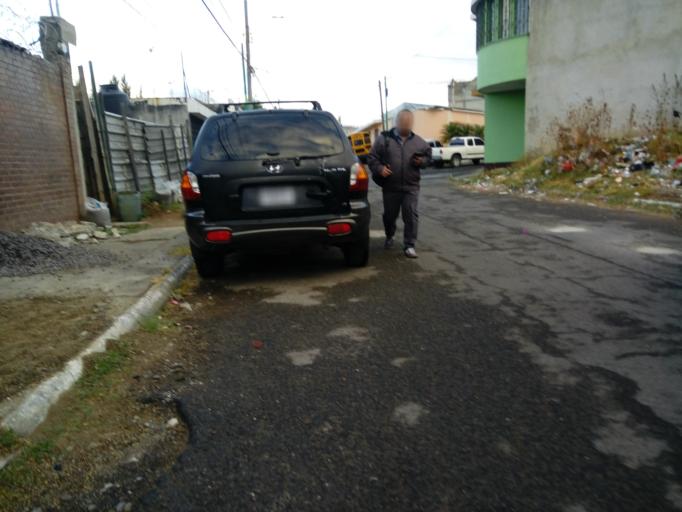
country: GT
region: Guatemala
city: Villa Nueva
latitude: 14.5322
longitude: -90.5814
